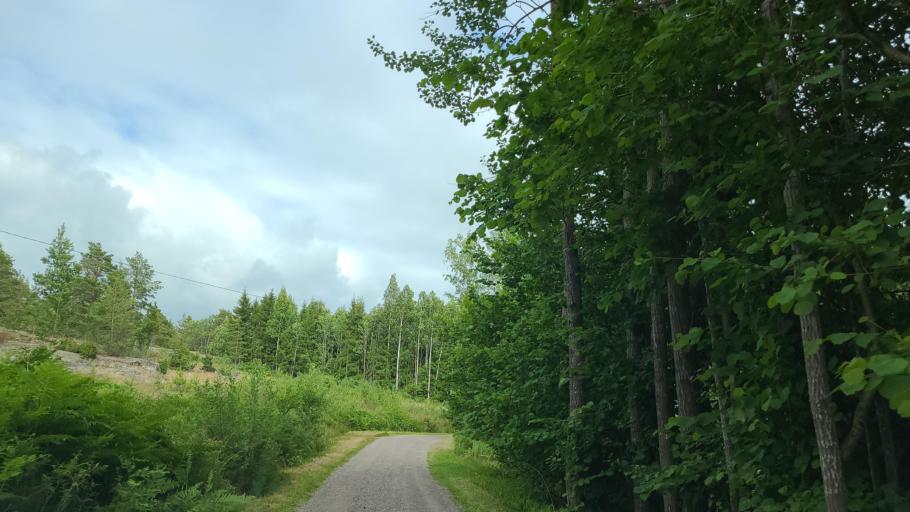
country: FI
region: Varsinais-Suomi
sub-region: Aboland-Turunmaa
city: Nagu
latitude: 60.1296
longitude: 21.8059
